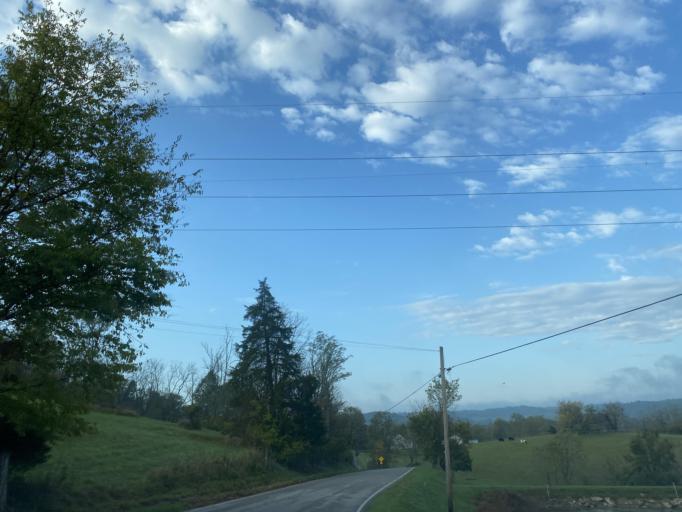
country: US
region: Kentucky
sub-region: Pendleton County
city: Falmouth
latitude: 38.7646
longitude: -84.3388
